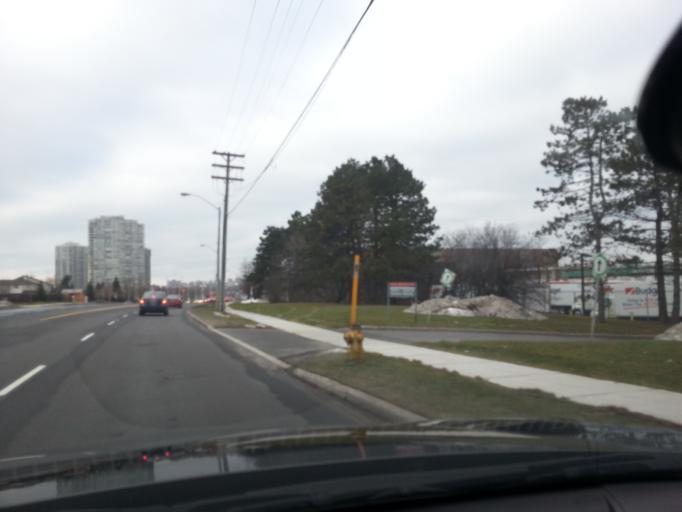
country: CA
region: Ontario
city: Ottawa
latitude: 45.4116
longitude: -75.6527
